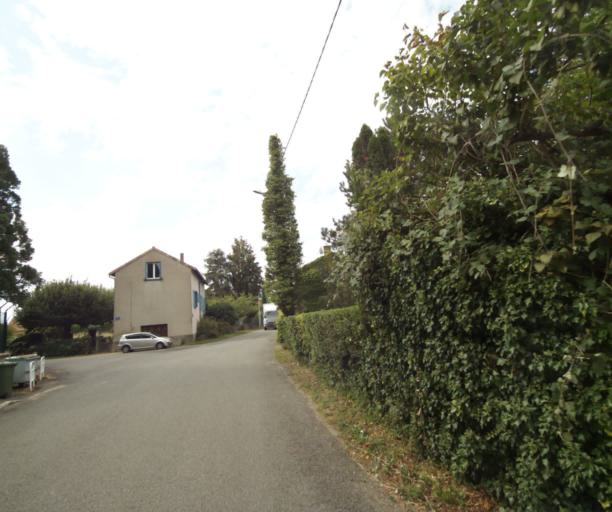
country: FR
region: Bourgogne
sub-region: Departement de Saone-et-Loire
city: Tournus
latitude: 46.5582
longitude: 4.9073
